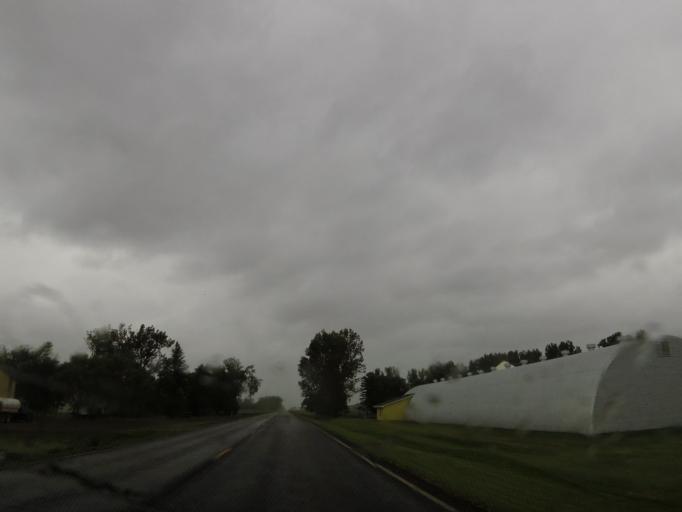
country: US
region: North Dakota
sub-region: Walsh County
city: Grafton
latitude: 48.4703
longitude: -97.4193
